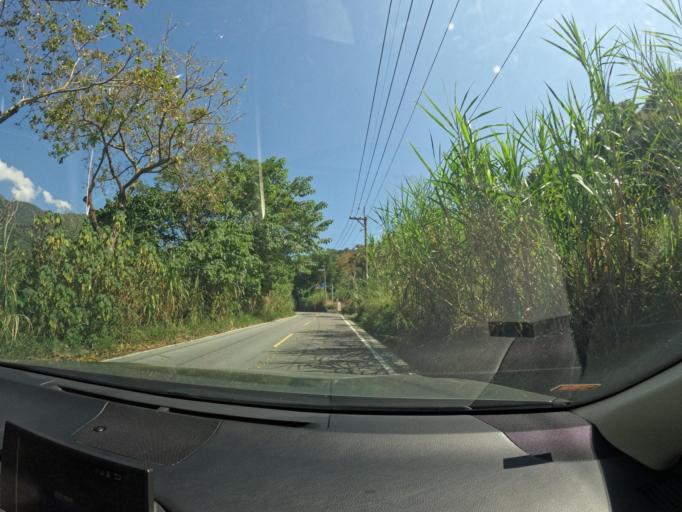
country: TW
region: Taiwan
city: Yujing
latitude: 23.1770
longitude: 120.7797
